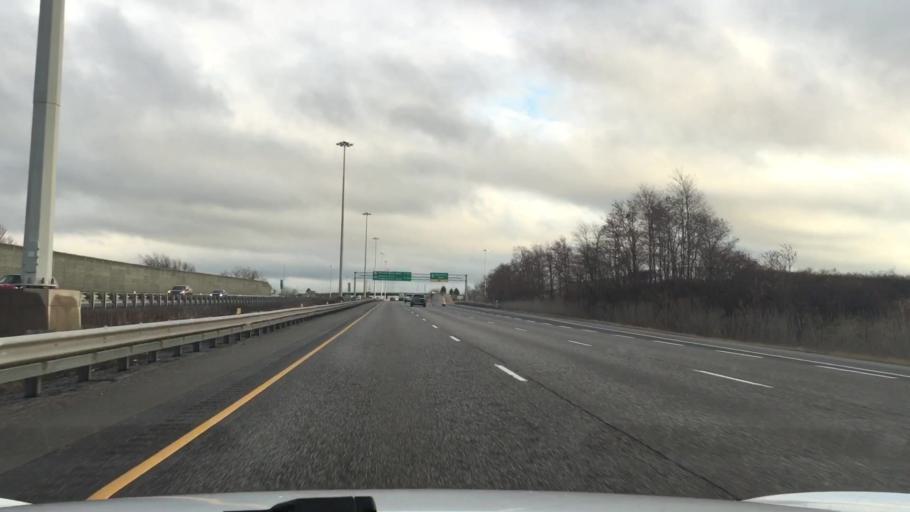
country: CA
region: Ontario
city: Thorold
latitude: 43.1406
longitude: -79.1373
